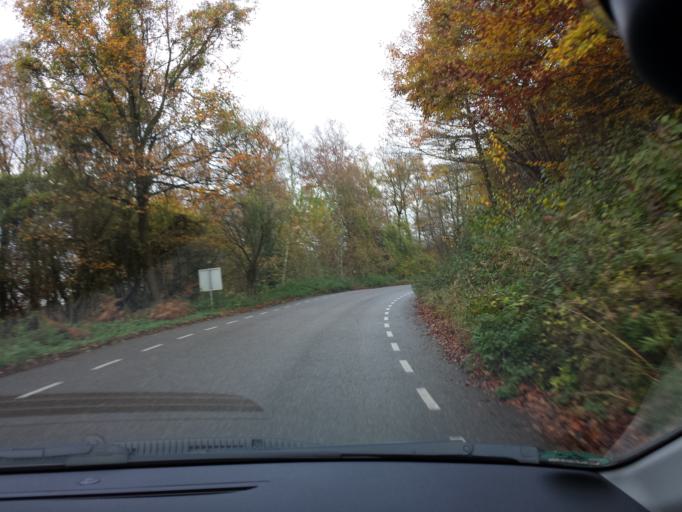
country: BE
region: Wallonia
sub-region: Province de Liege
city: Plombieres
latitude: 50.7647
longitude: 5.9534
